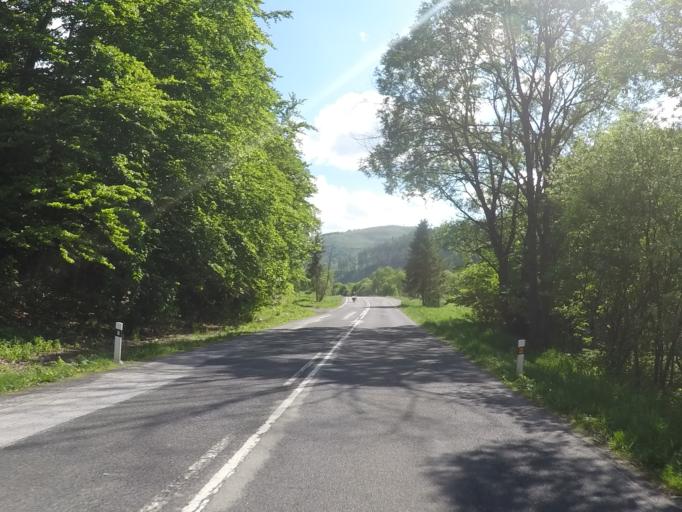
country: SK
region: Presovsky
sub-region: Okres Poprad
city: Poprad
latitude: 48.9757
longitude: 20.2993
